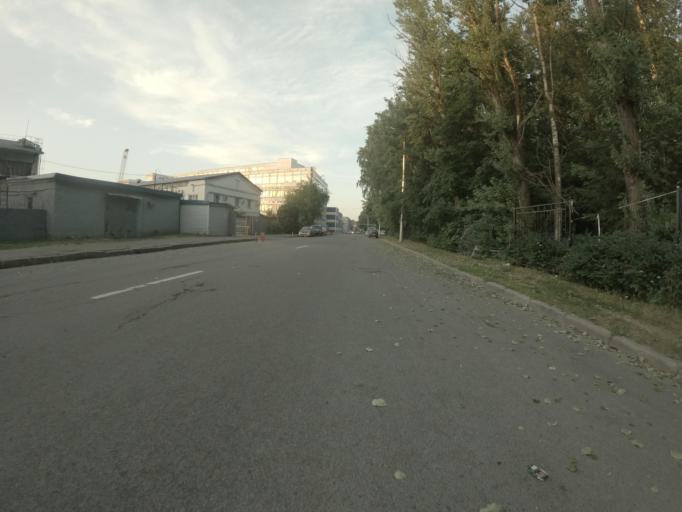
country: RU
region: St.-Petersburg
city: Krasnogvargeisky
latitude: 59.9504
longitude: 30.4256
